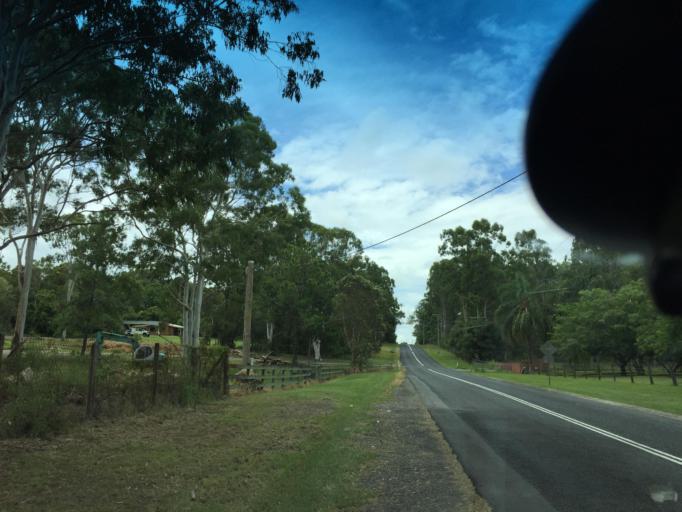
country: AU
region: Queensland
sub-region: Moreton Bay
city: Burpengary
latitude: -27.1451
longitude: 152.9617
